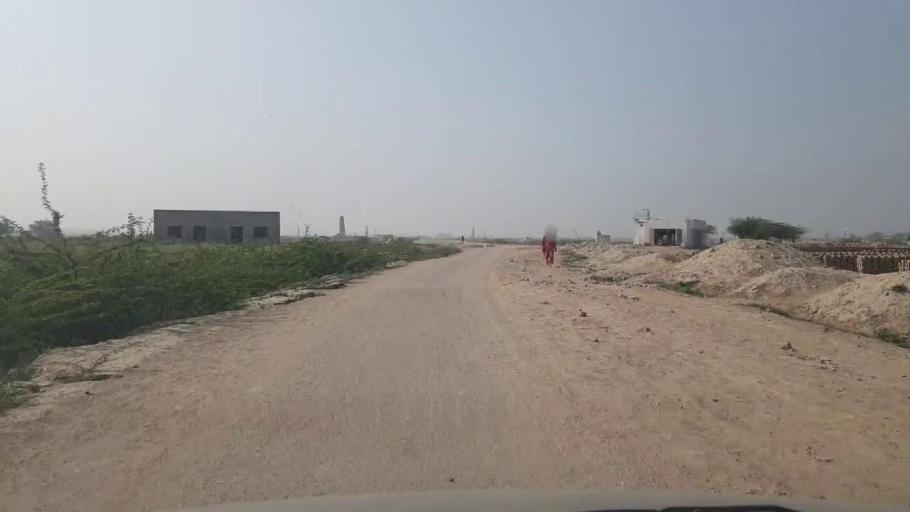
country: PK
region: Sindh
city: Umarkot
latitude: 25.3946
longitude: 69.7494
